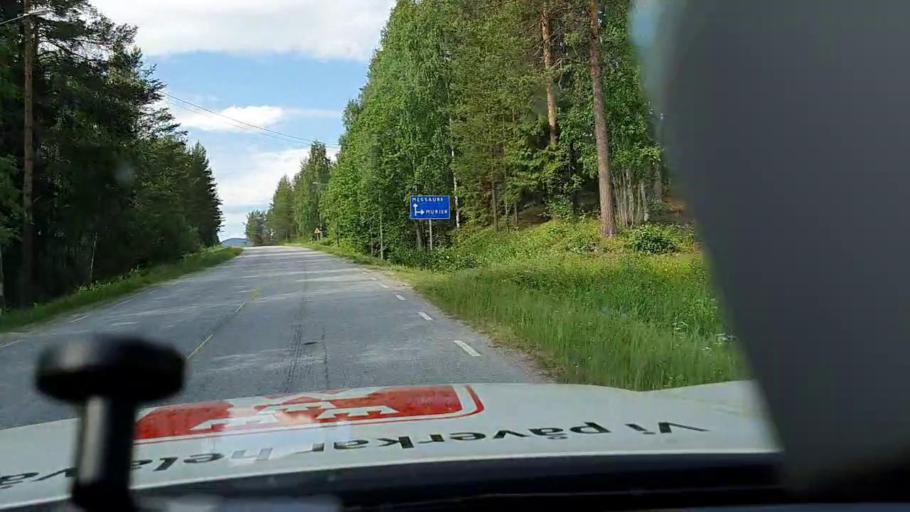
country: SE
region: Norrbotten
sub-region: Gallivare Kommun
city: Gaellivare
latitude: 66.4551
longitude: 20.6566
